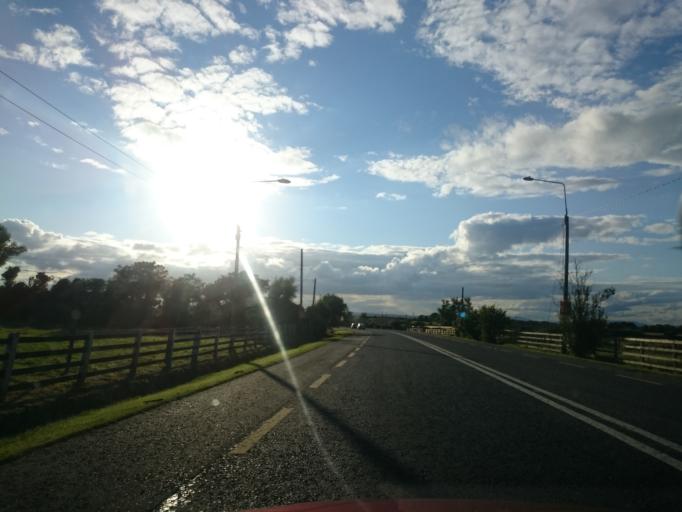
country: IE
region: Leinster
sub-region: Loch Garman
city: Ballygerry
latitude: 52.2430
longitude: -6.3588
